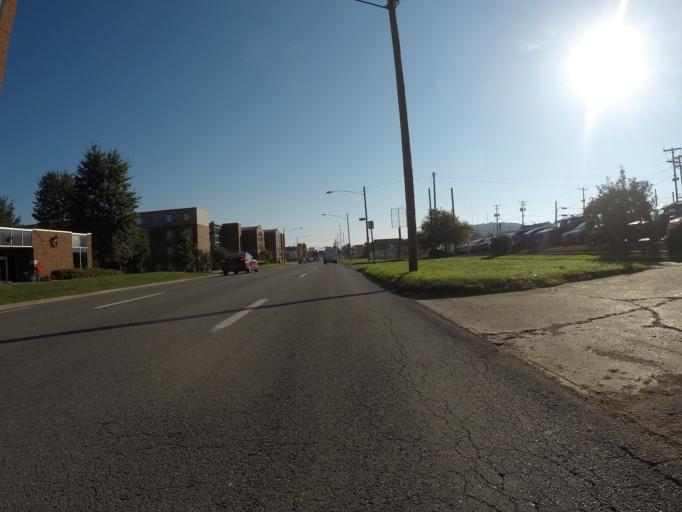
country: US
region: West Virginia
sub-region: Cabell County
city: Huntington
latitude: 38.4225
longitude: -82.4250
